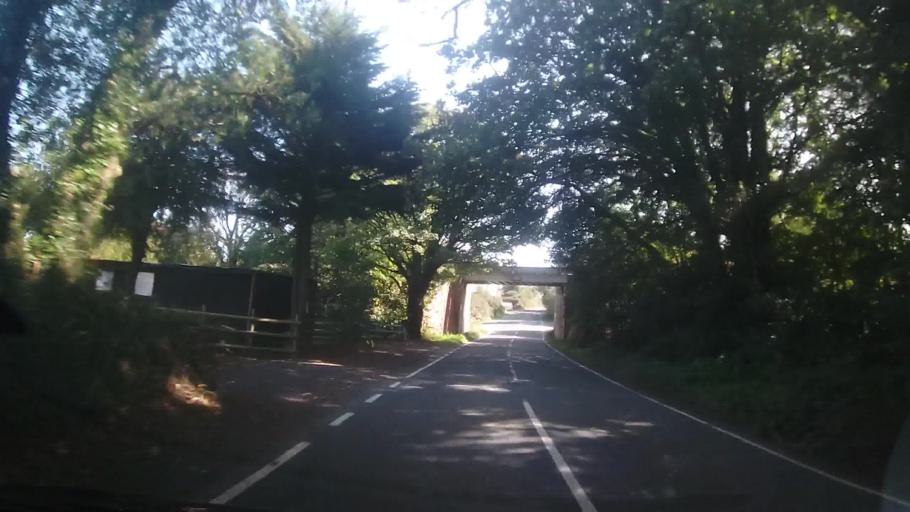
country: GB
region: Wales
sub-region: Pembrokeshire
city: Scleddau
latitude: 51.9359
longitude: -5.0158
